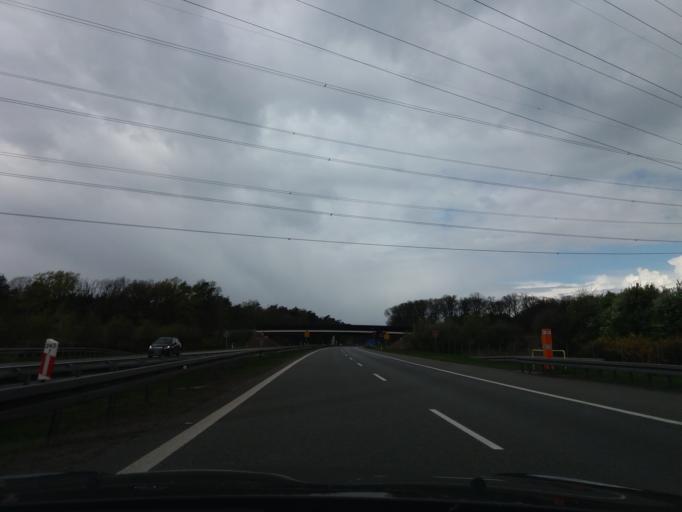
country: PL
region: Opole Voivodeship
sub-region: Powiat opolski
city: Proszkow
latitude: 50.5324
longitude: 17.9101
